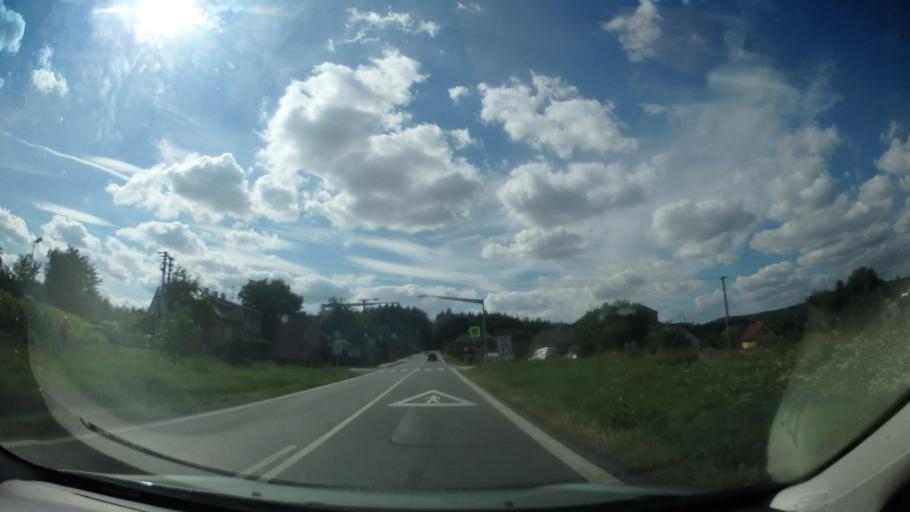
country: CZ
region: Vysocina
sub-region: Okres Zd'ar nad Sazavou
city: Zd'ar nad Sazavou
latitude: 49.5620
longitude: 15.9030
